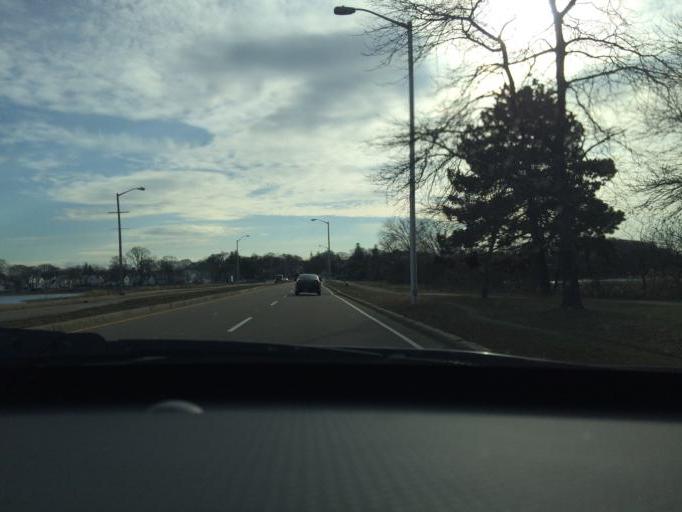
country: US
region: Massachusetts
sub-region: Norfolk County
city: Quincy
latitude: 42.2681
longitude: -70.9970
